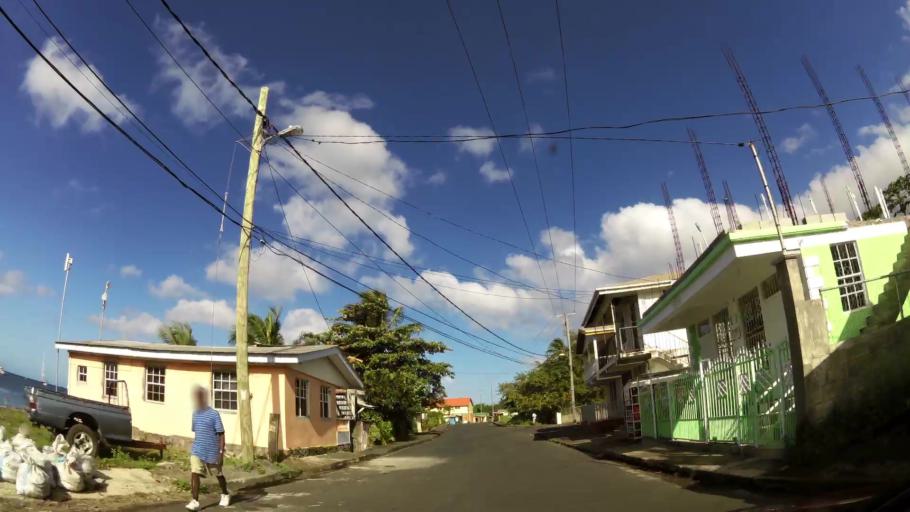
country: DM
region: Saint John
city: Portsmouth
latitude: 15.5797
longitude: -61.4584
